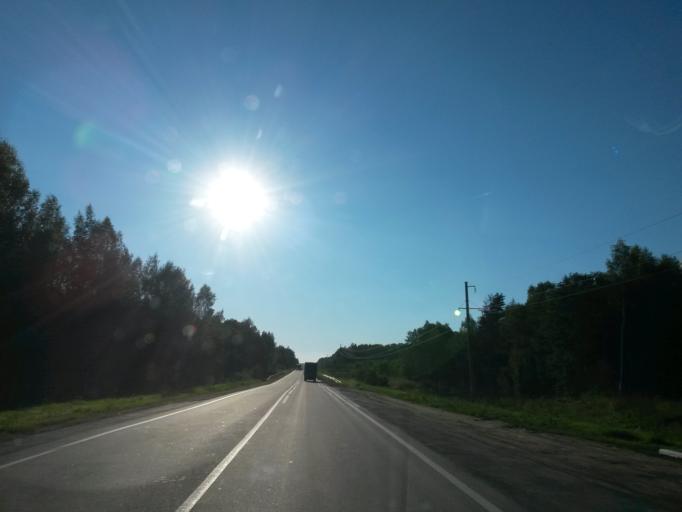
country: RU
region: Jaroslavl
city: Dubki
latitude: 57.2584
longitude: 40.0741
